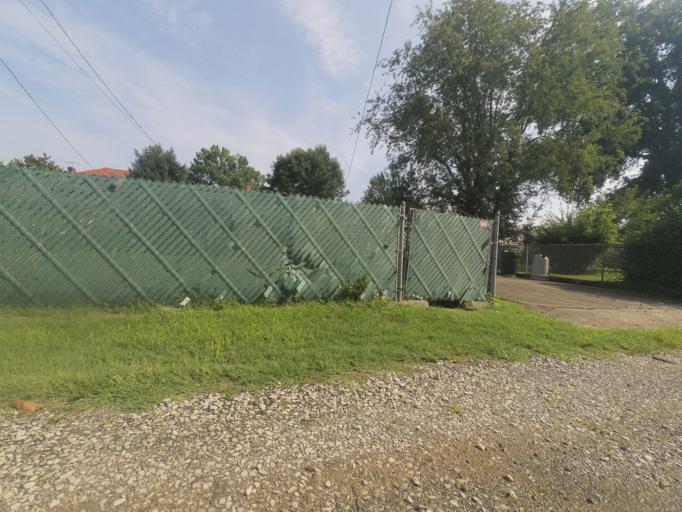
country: US
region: West Virginia
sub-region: Cabell County
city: Huntington
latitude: 38.4090
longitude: -82.4491
